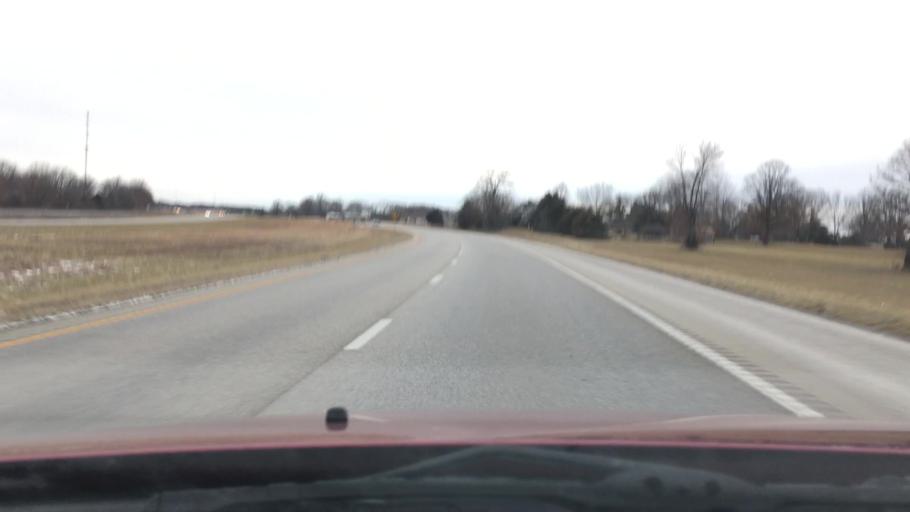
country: US
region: Missouri
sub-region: Webster County
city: Seymour
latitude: 37.1687
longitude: -92.8073
